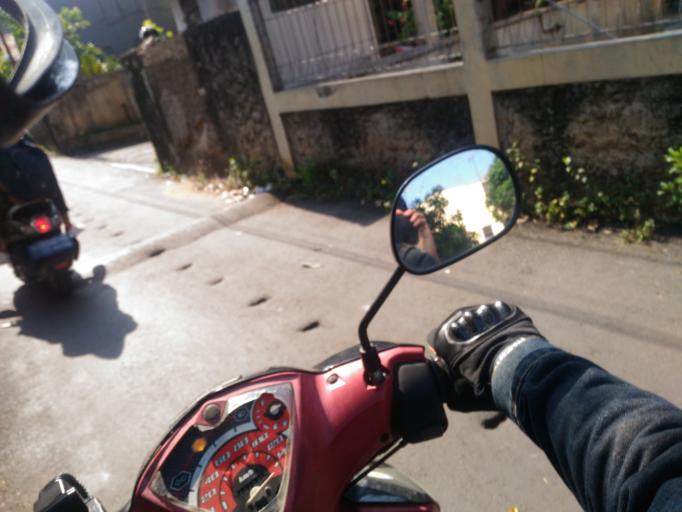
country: ID
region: West Java
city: Depok
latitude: -6.3583
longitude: 106.8337
